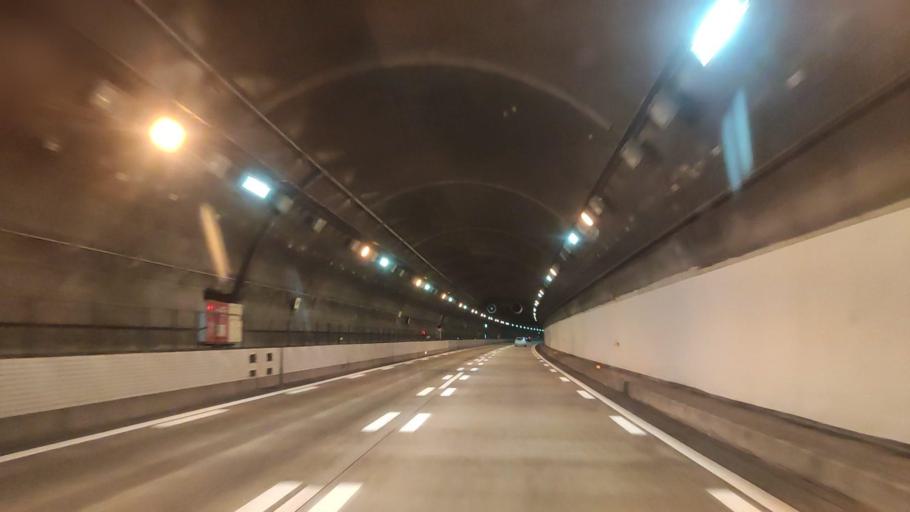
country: JP
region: Hiroshima
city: Fukuyama
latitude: 34.4968
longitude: 133.3184
